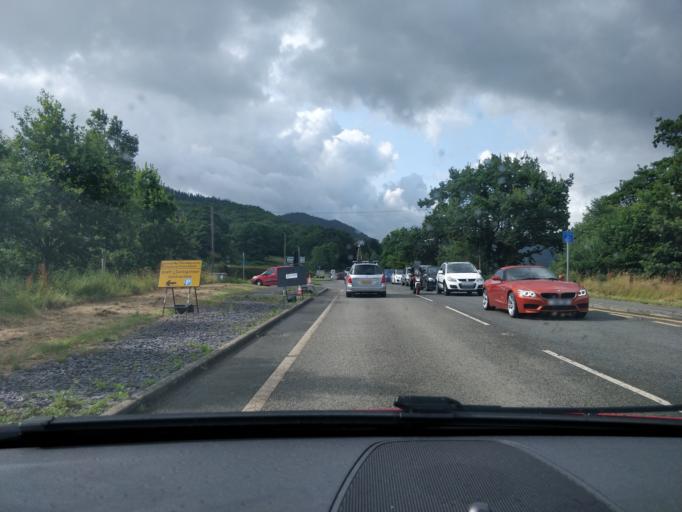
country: GB
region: Wales
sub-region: Conwy
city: Betws-y-Coed
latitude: 53.1115
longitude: -3.7824
